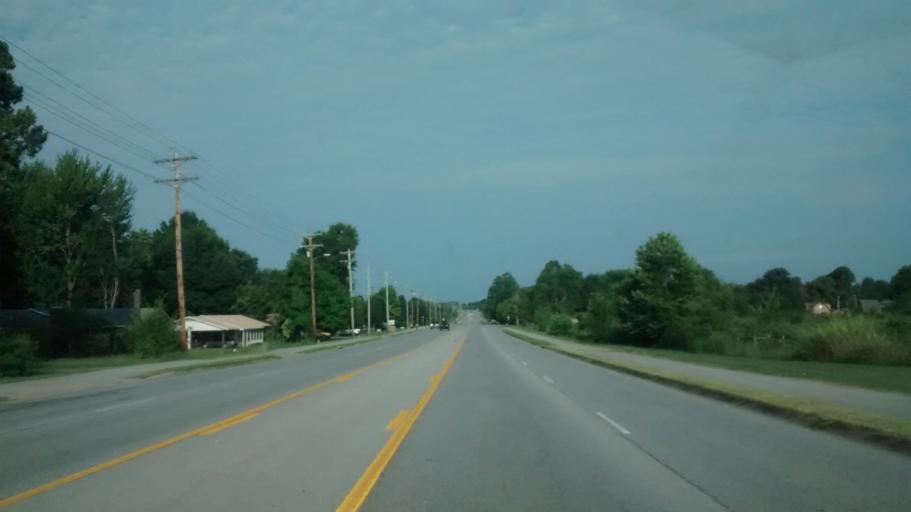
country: US
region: Arkansas
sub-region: Washington County
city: Farmington
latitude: 36.0791
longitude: -94.2370
